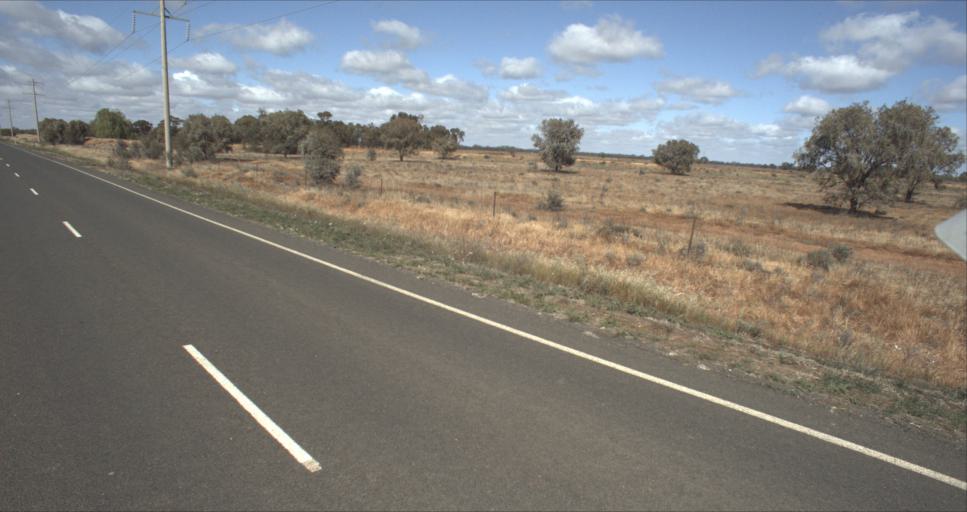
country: AU
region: New South Wales
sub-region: Murrumbidgee Shire
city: Darlington Point
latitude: -34.5264
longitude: 146.1748
